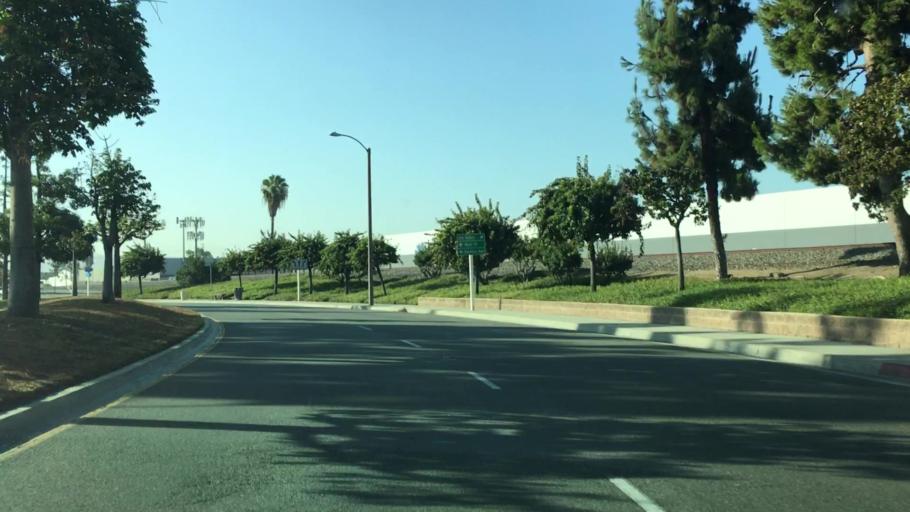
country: US
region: California
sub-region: Los Angeles County
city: La Puente
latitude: 34.0208
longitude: -117.9551
